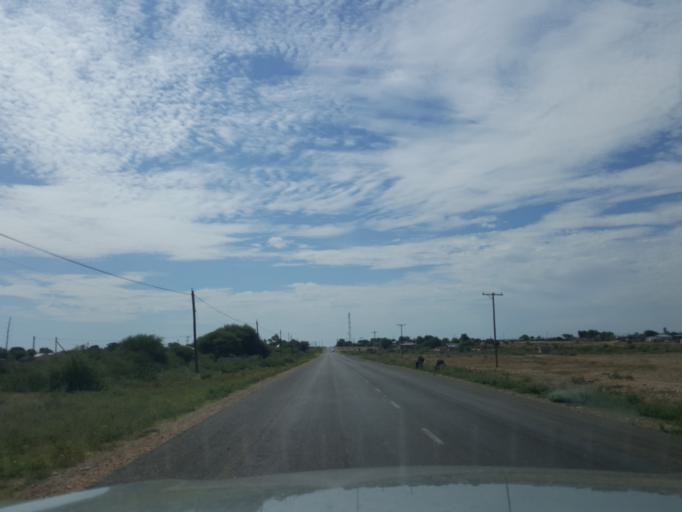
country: BW
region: Kweneng
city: Letlhakeng
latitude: -24.1107
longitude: 25.0349
